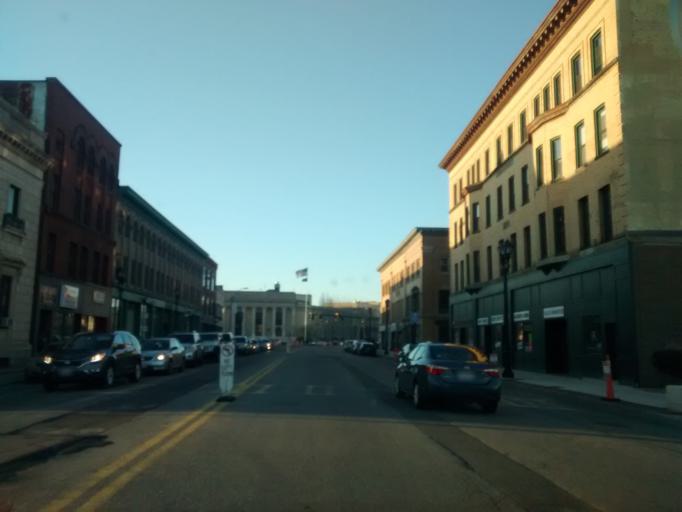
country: US
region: Massachusetts
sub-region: Middlesex County
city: Framingham
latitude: 42.2779
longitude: -71.4168
